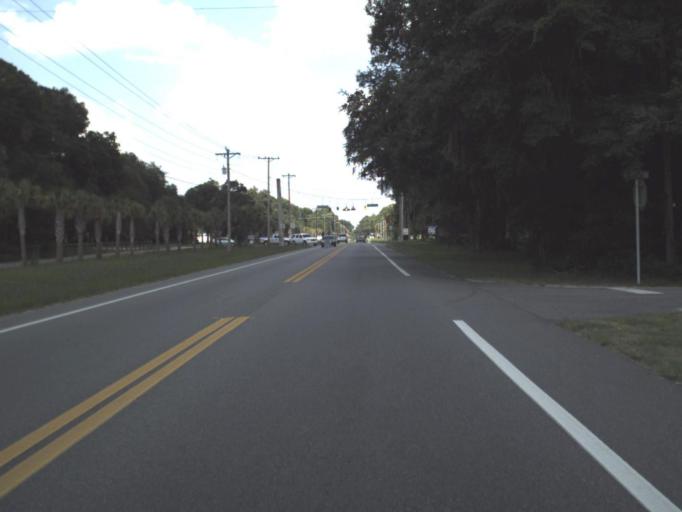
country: US
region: Florida
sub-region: Putnam County
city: Interlachen
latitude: 29.7325
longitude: -81.8893
